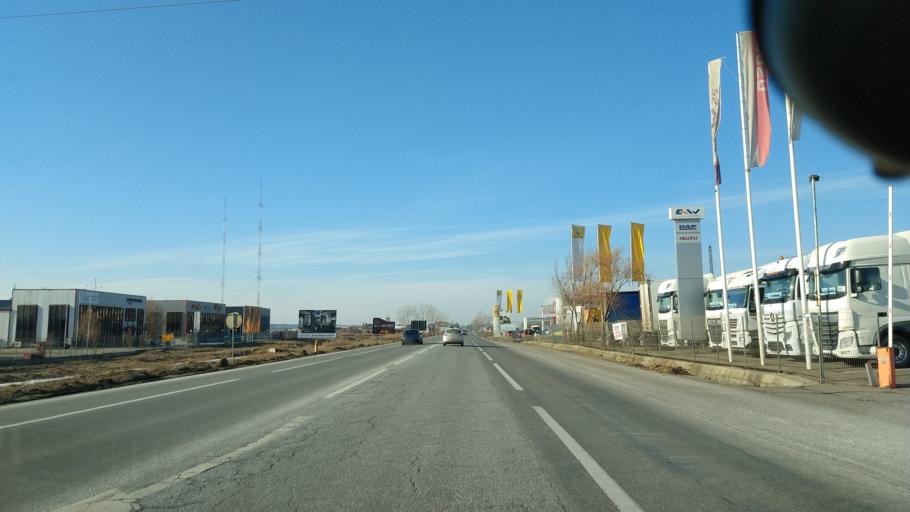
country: RO
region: Iasi
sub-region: Comuna Valea Lupului
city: Valea Lupului
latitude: 47.1822
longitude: 27.4671
